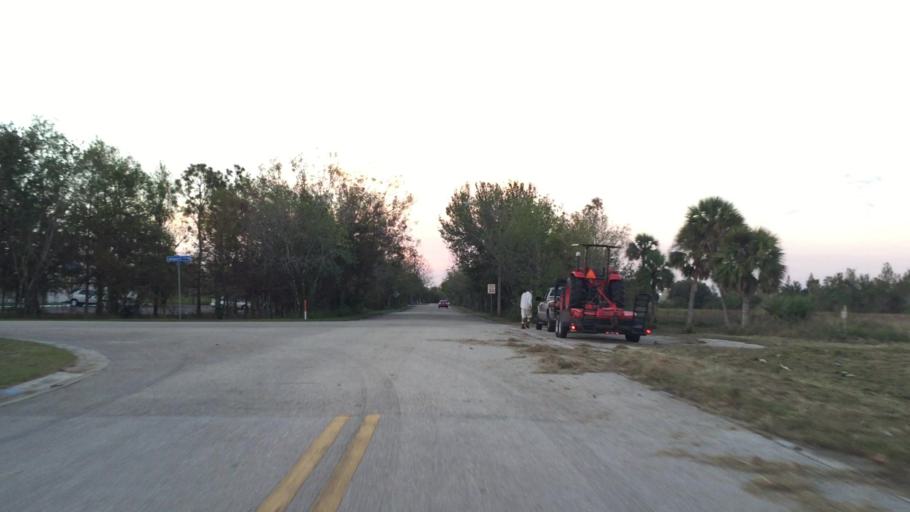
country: US
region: Florida
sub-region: Lee County
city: Gateway
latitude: 26.5336
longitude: -81.7915
